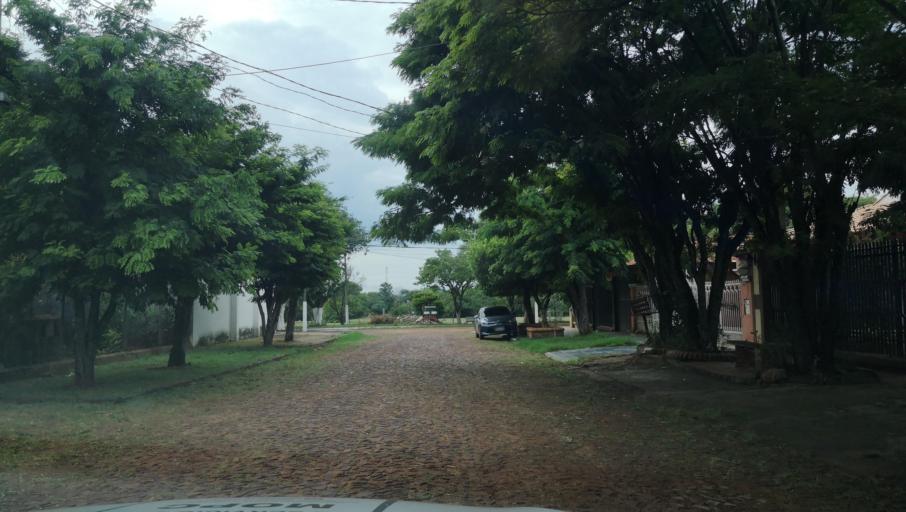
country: PY
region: Misiones
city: Santa Maria
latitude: -26.8867
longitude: -57.0375
